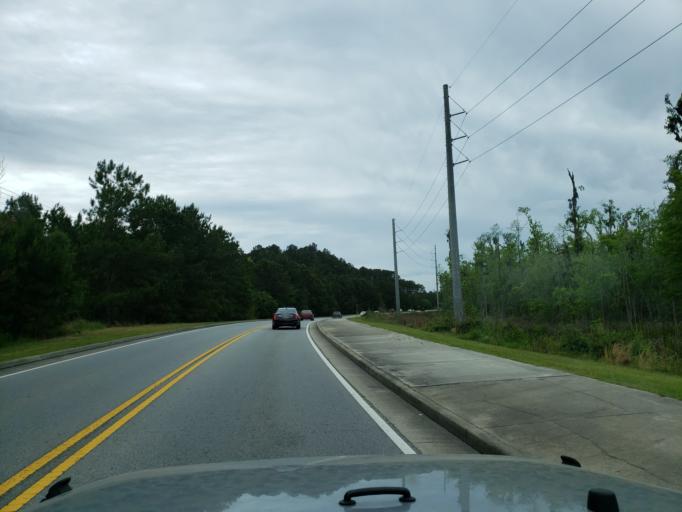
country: US
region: Georgia
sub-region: Chatham County
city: Pooler
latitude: 32.1599
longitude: -81.2332
